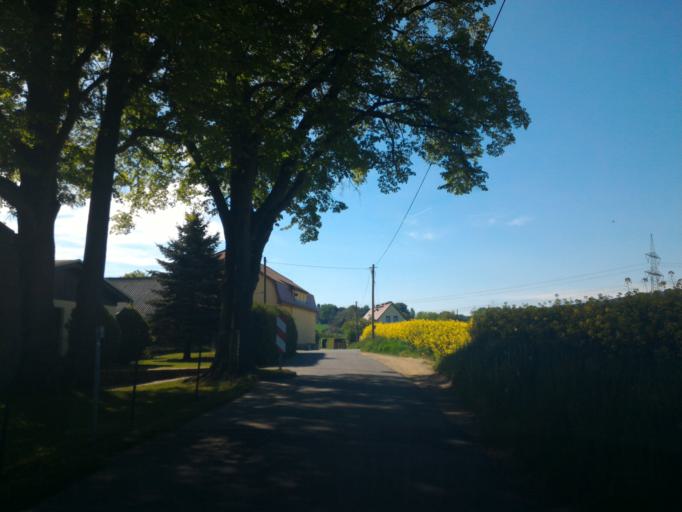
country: DE
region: Saxony
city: Niedercunnersdorf
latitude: 51.0440
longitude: 14.6632
